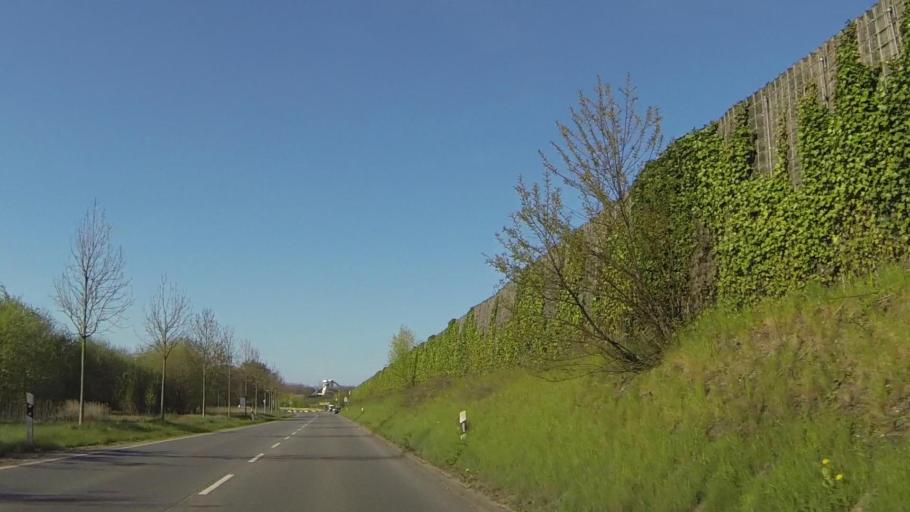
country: DE
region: Schleswig-Holstein
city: Pinneberg
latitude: 53.6561
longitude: 9.7729
